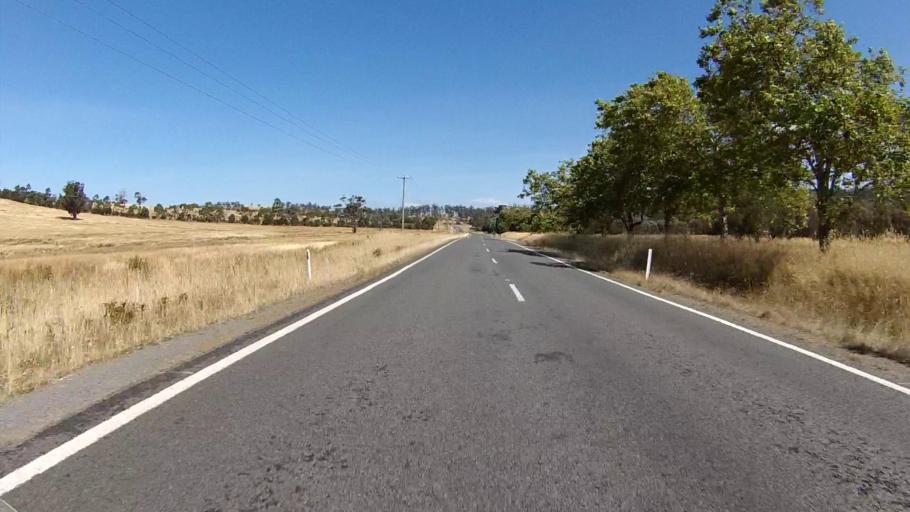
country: AU
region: Tasmania
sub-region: Sorell
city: Sorell
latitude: -42.4602
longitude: 147.9257
